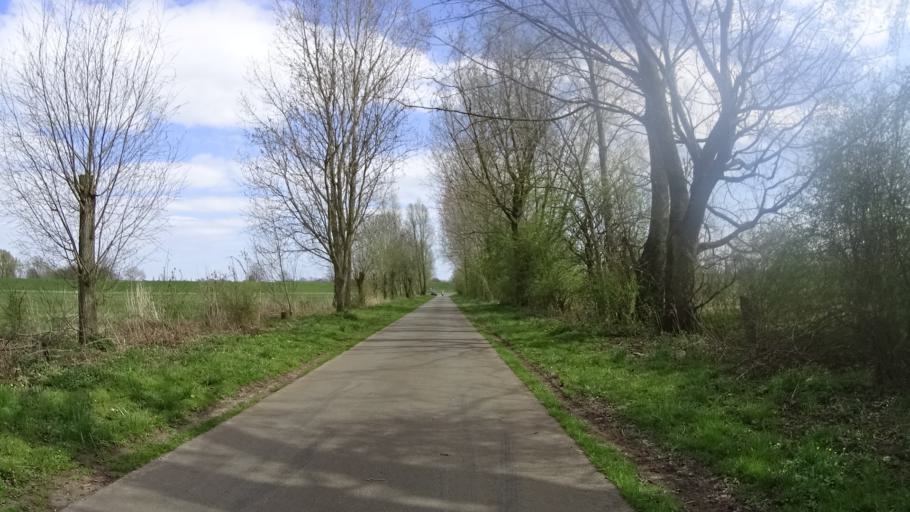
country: DE
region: Lower Saxony
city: Rhede
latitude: 53.0528
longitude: 7.3137
